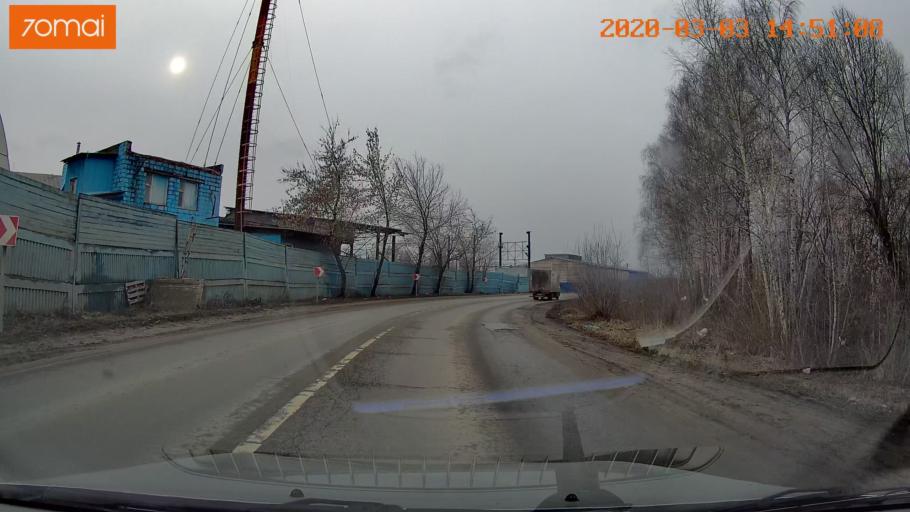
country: RU
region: Moskovskaya
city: Malakhovka
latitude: 55.6660
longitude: 38.0334
